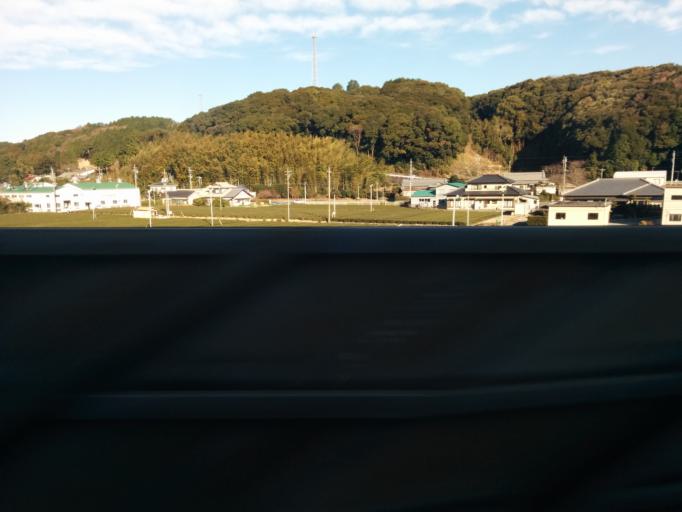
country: JP
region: Shizuoka
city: Shimada
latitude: 34.8007
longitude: 138.1950
